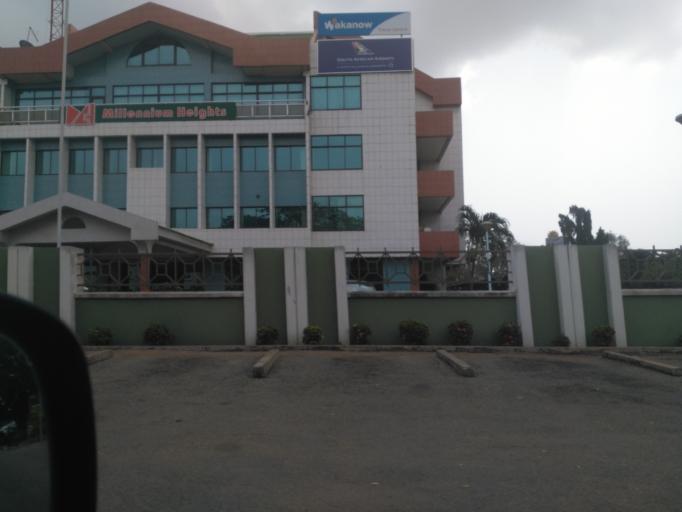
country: GH
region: Greater Accra
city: Accra
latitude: 5.5988
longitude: -0.1807
